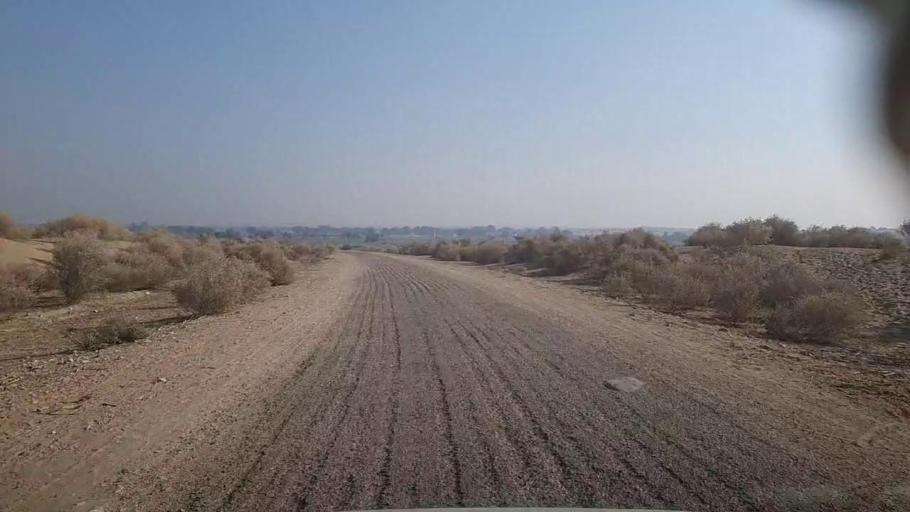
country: PK
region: Sindh
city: Kandiari
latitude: 26.8226
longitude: 68.4900
